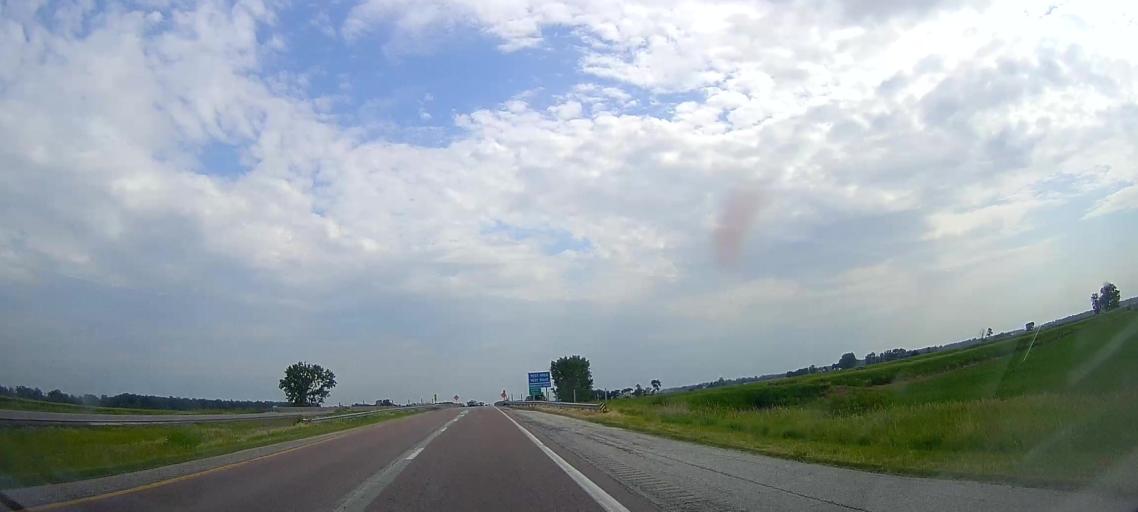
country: US
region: Nebraska
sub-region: Burt County
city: Tekamah
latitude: 41.7519
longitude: -96.0462
